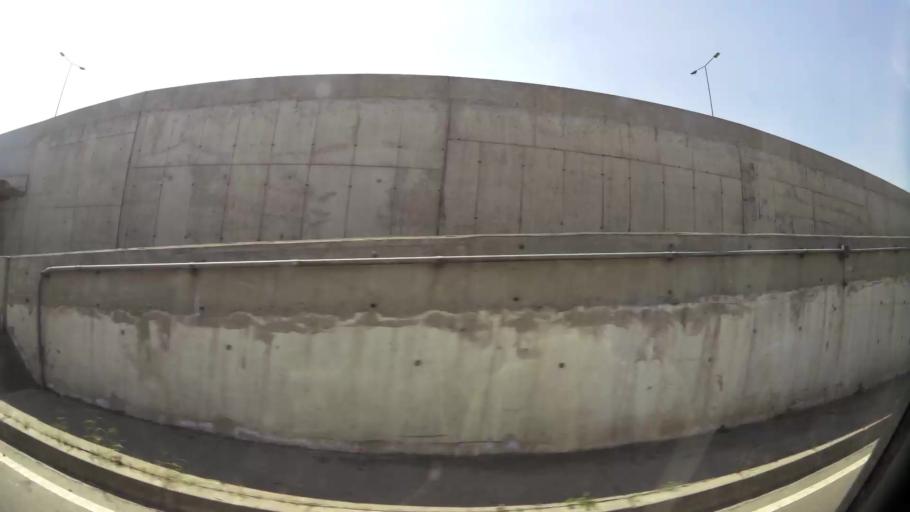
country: CL
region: Santiago Metropolitan
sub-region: Provincia de Santiago
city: Santiago
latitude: -33.4278
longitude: -70.6667
